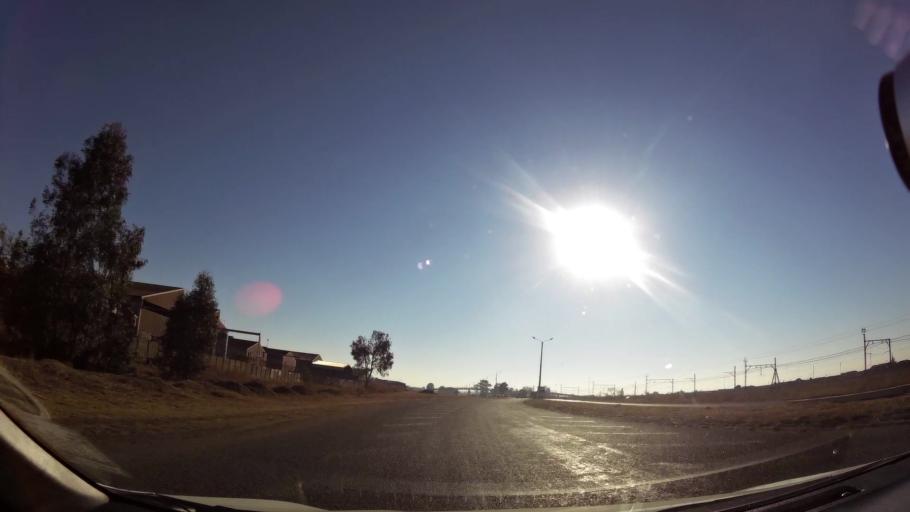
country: ZA
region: Gauteng
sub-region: Ekurhuleni Metropolitan Municipality
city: Germiston
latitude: -26.3532
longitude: 28.1234
